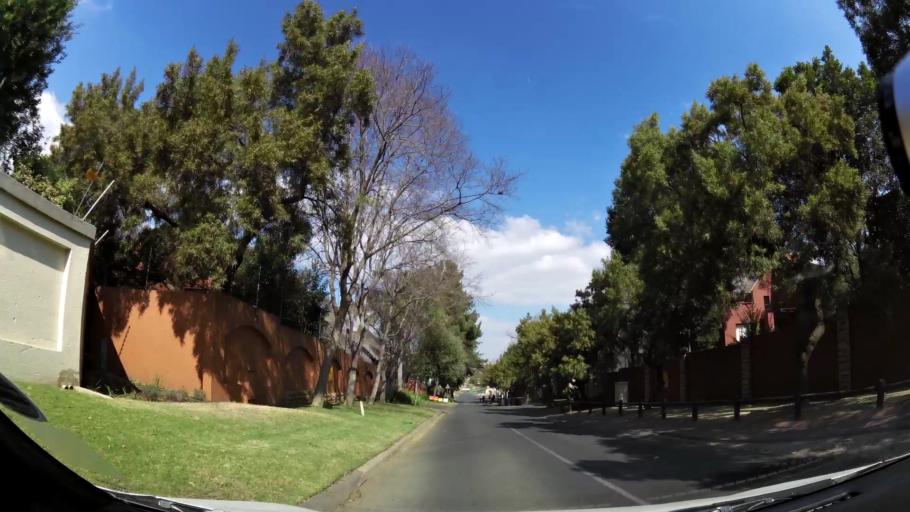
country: ZA
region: Gauteng
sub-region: City of Johannesburg Metropolitan Municipality
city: Midrand
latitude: -26.0284
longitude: 28.0669
